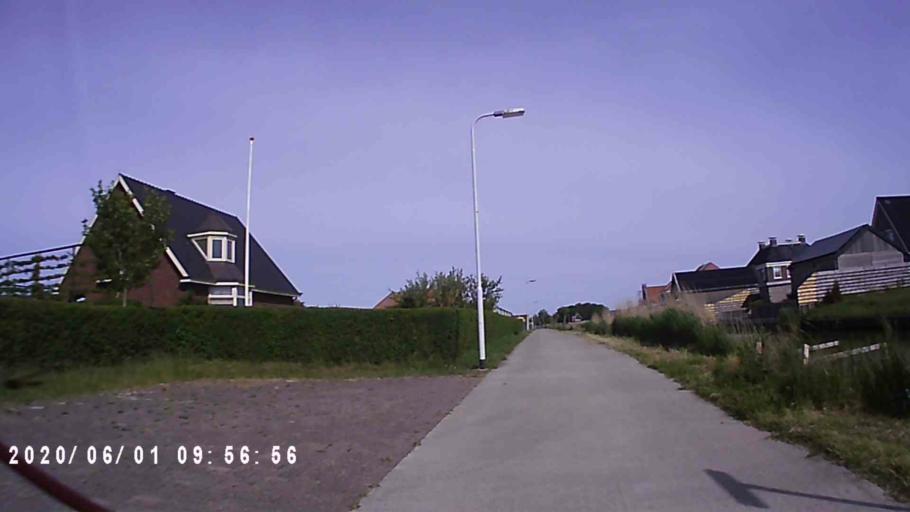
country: NL
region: Friesland
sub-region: Menameradiel
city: Berltsum
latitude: 53.2376
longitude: 5.6473
